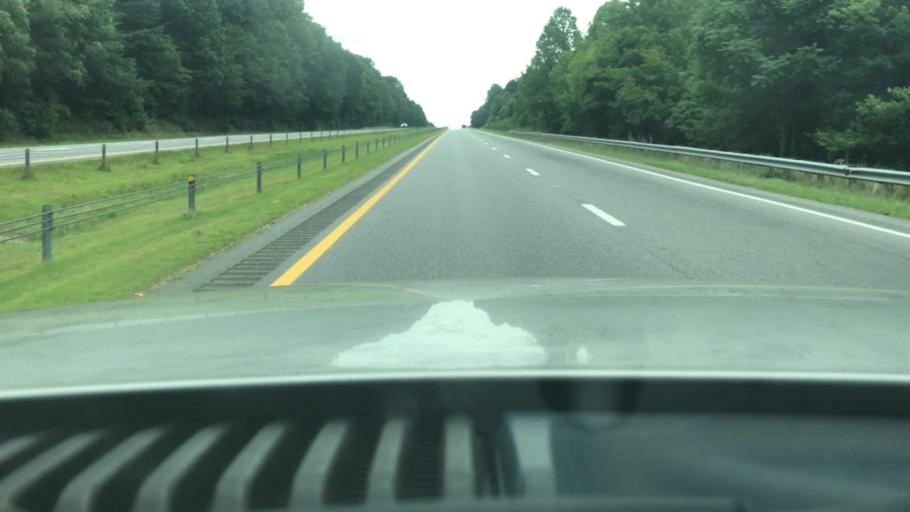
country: US
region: North Carolina
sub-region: Wilkes County
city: North Wilkesboro
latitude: 36.1457
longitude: -81.0509
